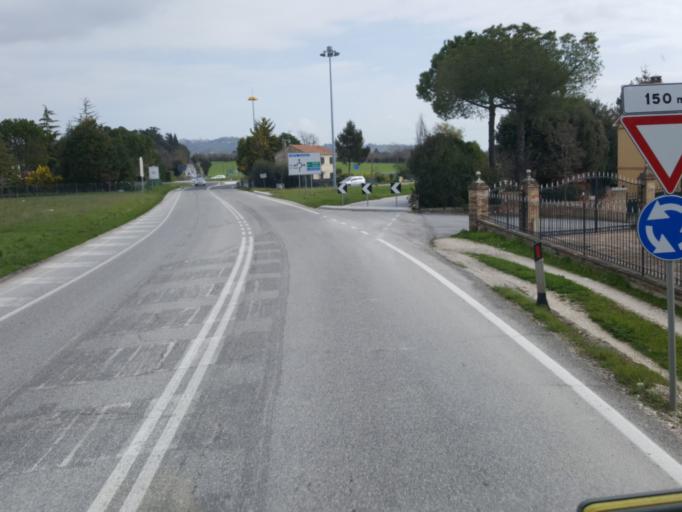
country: IT
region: The Marches
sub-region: Provincia di Macerata
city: Recanati
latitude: 43.3649
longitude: 13.5116
